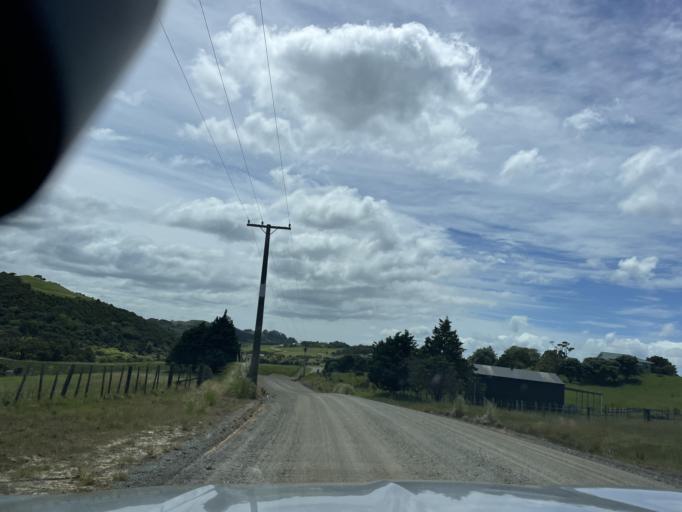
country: NZ
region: Auckland
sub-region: Auckland
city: Wellsford
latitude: -36.1720
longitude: 174.2733
